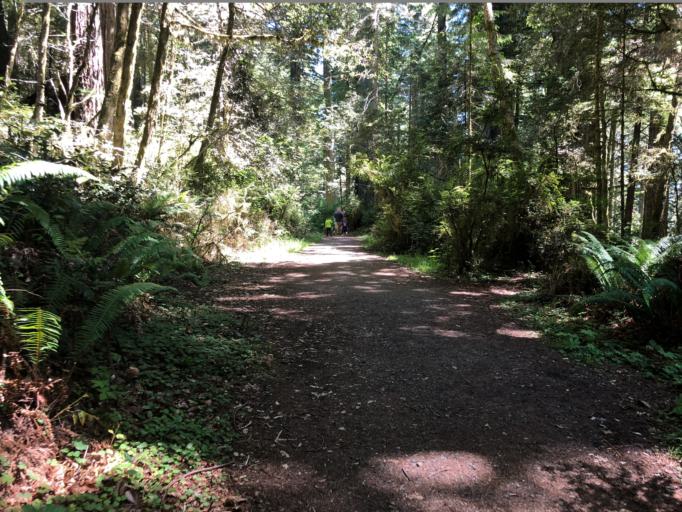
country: US
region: California
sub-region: Humboldt County
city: Westhaven-Moonstone
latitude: 41.3079
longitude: -124.0238
